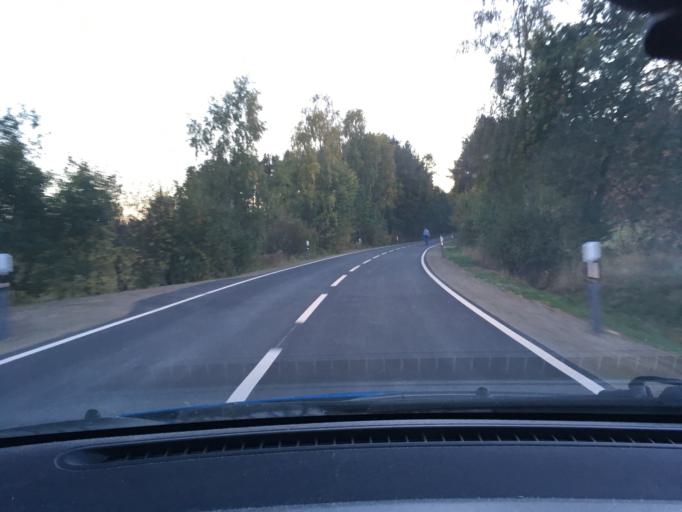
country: DE
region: Lower Saxony
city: Neetze
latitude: 53.2591
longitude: 10.6139
